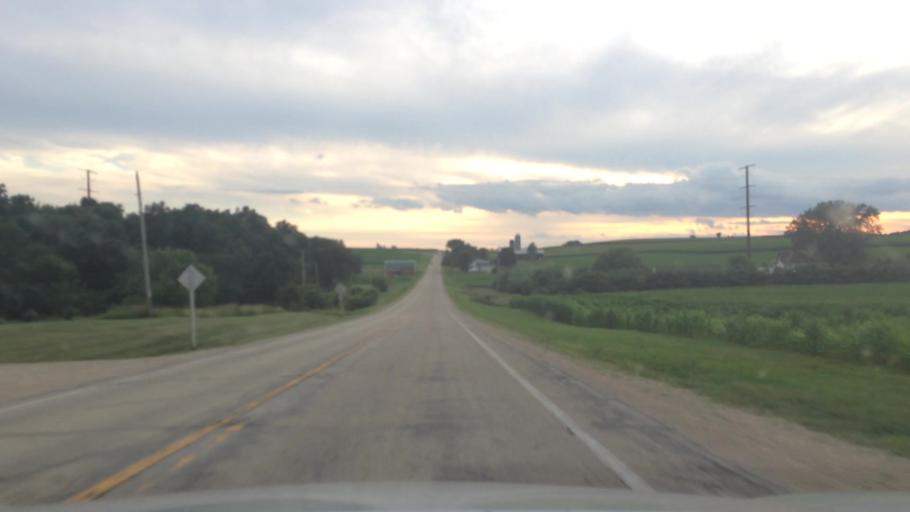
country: US
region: Wisconsin
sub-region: Columbia County
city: Lodi
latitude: 43.2358
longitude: -89.5265
